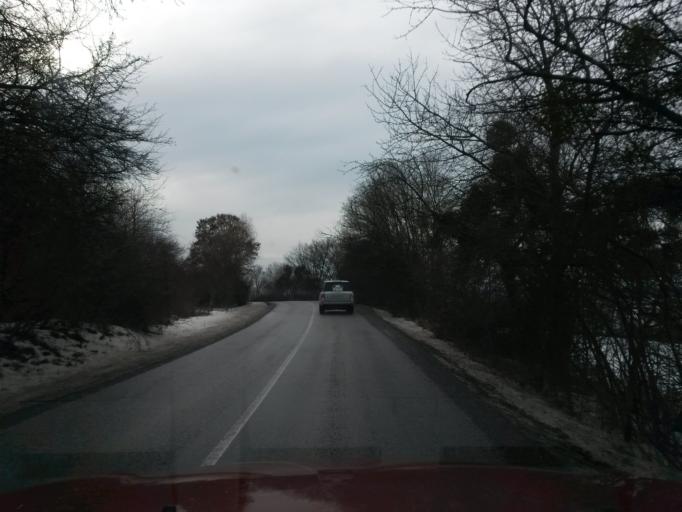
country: SK
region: Kosicky
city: Kosice
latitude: 48.7699
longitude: 21.3685
